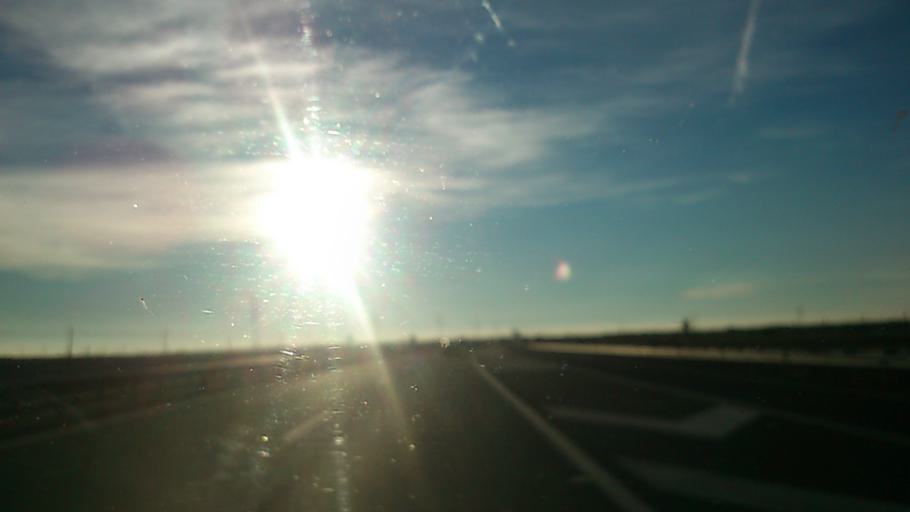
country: ES
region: Castille-La Mancha
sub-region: Provincia de Guadalajara
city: Ledanca
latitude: 40.8576
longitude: -2.8397
